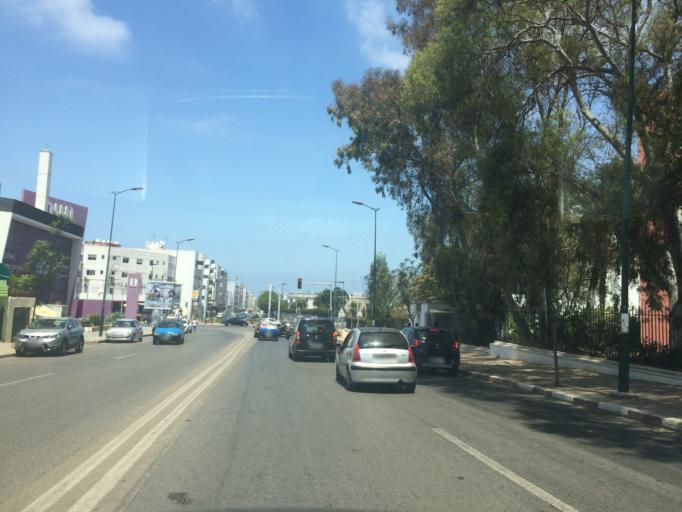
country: MA
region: Rabat-Sale-Zemmour-Zaer
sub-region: Rabat
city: Rabat
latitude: 33.9980
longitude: -6.8435
